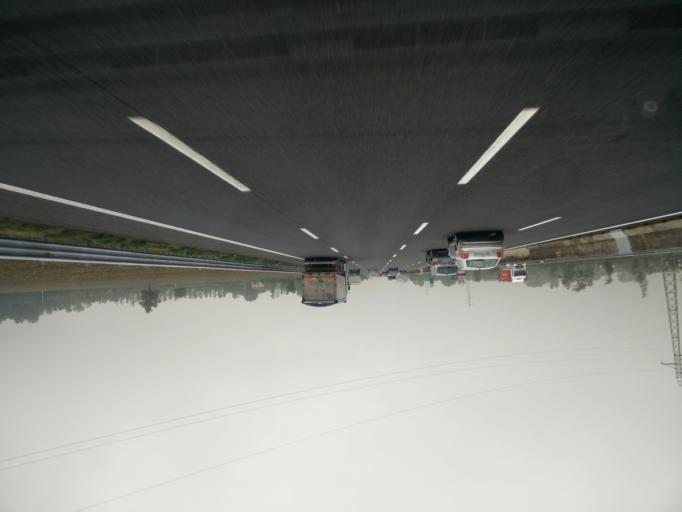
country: IT
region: Emilia-Romagna
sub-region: Provincia di Modena
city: San Damaso
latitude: 44.5942
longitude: 10.9420
